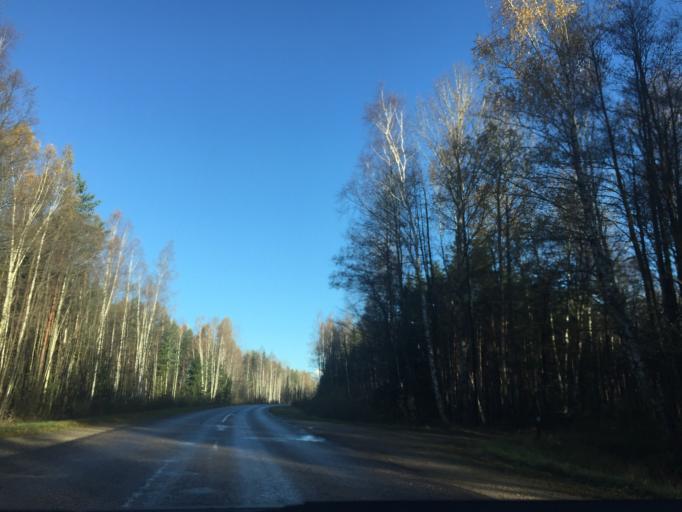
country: LV
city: Tireli
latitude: 56.9179
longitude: 23.5245
